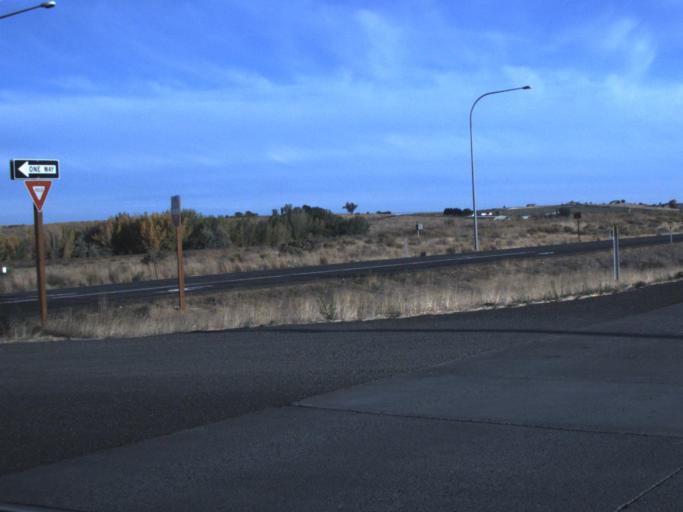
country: US
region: Washington
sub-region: Franklin County
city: Pasco
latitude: 46.4314
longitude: -119.0246
